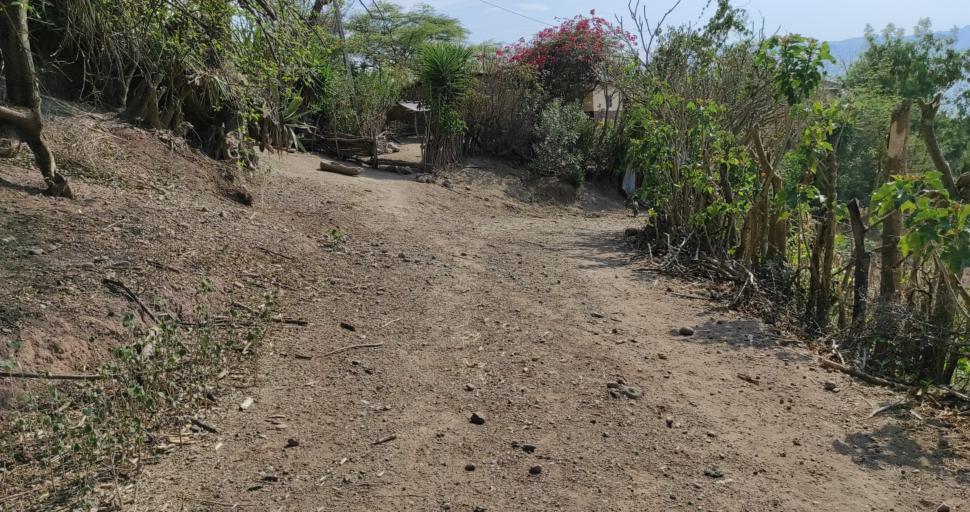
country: EC
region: Loja
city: Catacocha
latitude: -4.0037
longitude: -79.7137
